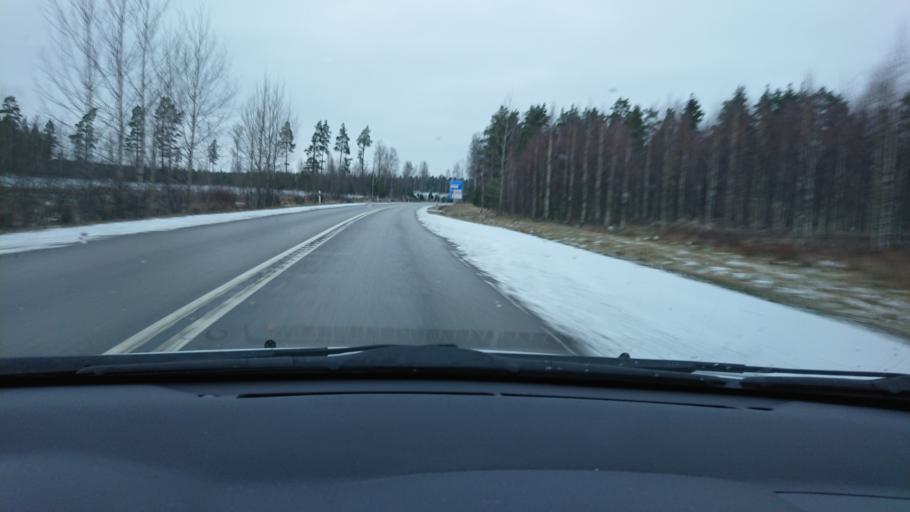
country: SE
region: Kalmar
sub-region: Hultsfreds Kommun
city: Hultsfred
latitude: 57.4973
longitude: 15.8209
